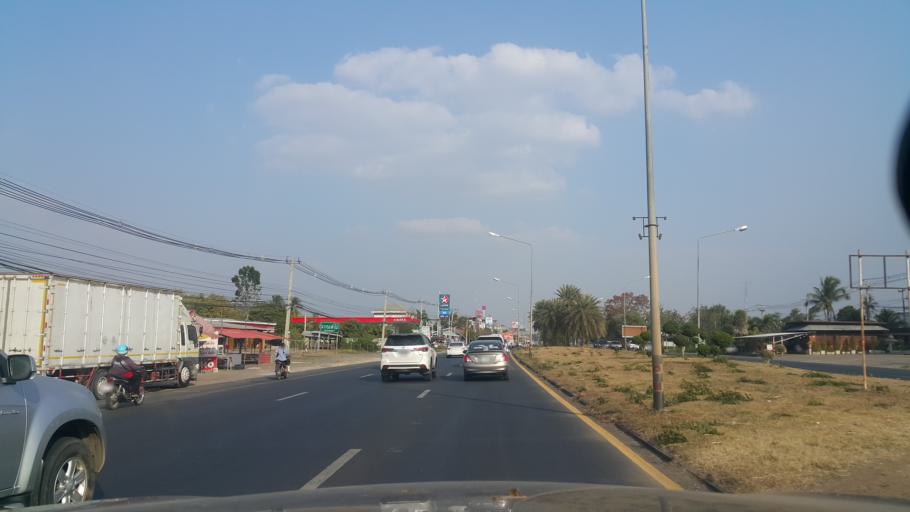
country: TH
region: Buriram
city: Nang Rong
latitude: 14.6332
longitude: 102.8034
